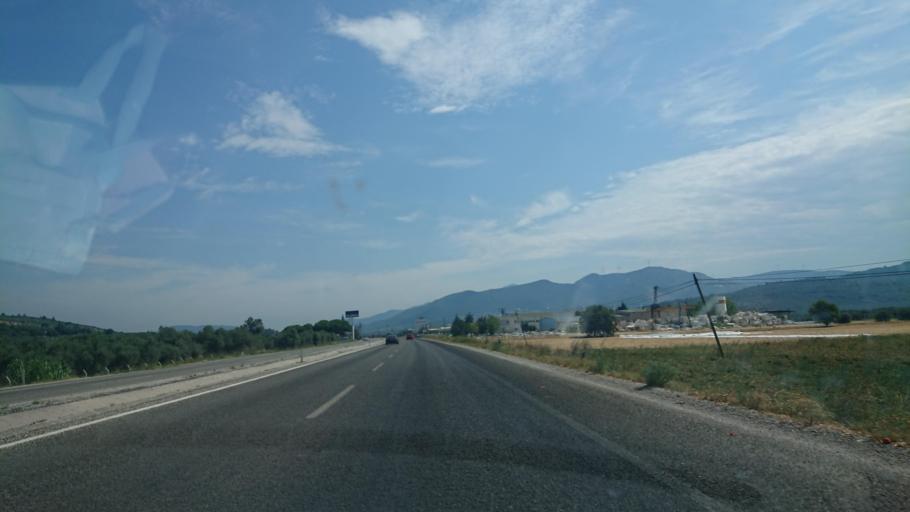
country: TR
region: Izmir
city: Dagkizilca
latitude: 38.2519
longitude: 27.3836
